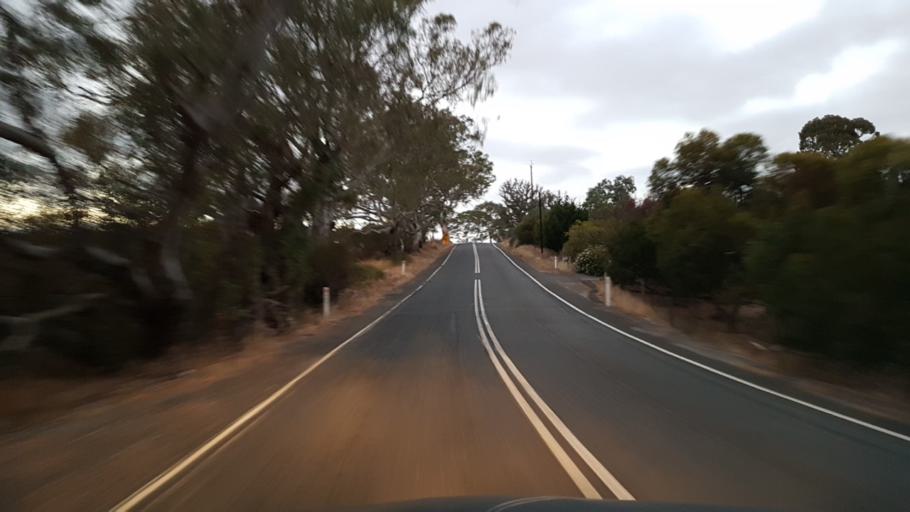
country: AU
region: South Australia
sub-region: Mount Barker
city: Nairne
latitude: -35.0300
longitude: 138.9581
